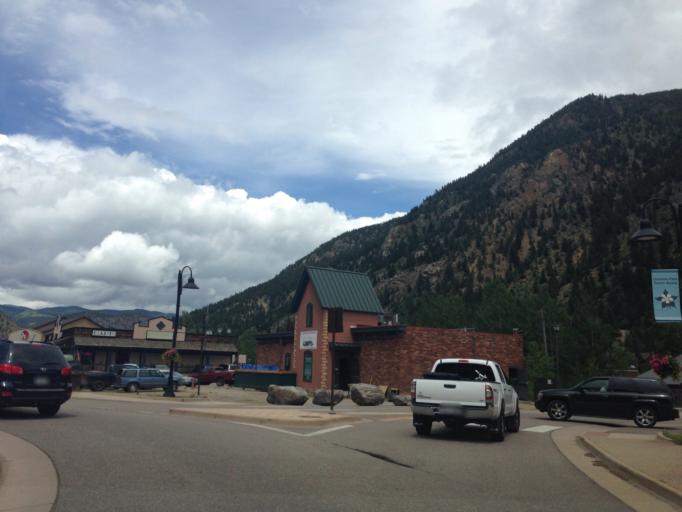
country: US
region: Colorado
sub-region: Clear Creek County
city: Georgetown
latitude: 39.7151
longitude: -105.6951
